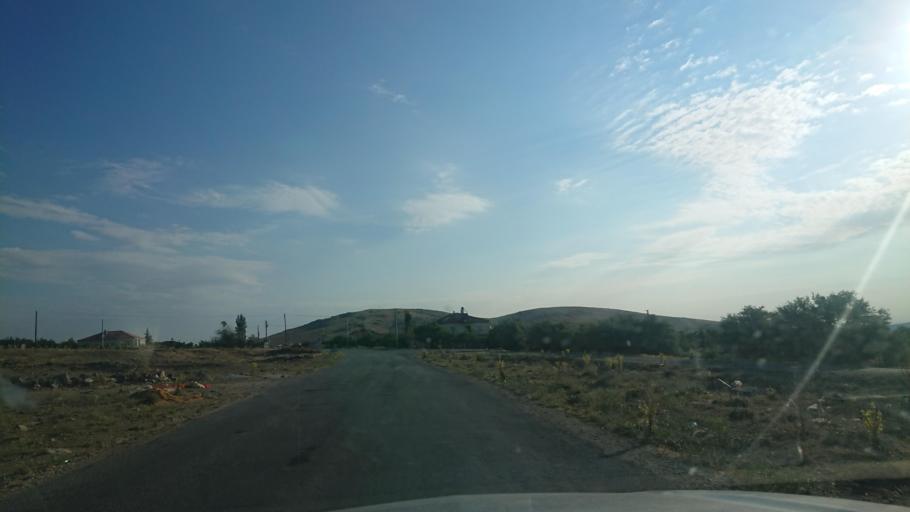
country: TR
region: Aksaray
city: Ortakoy
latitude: 38.7611
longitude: 34.0607
